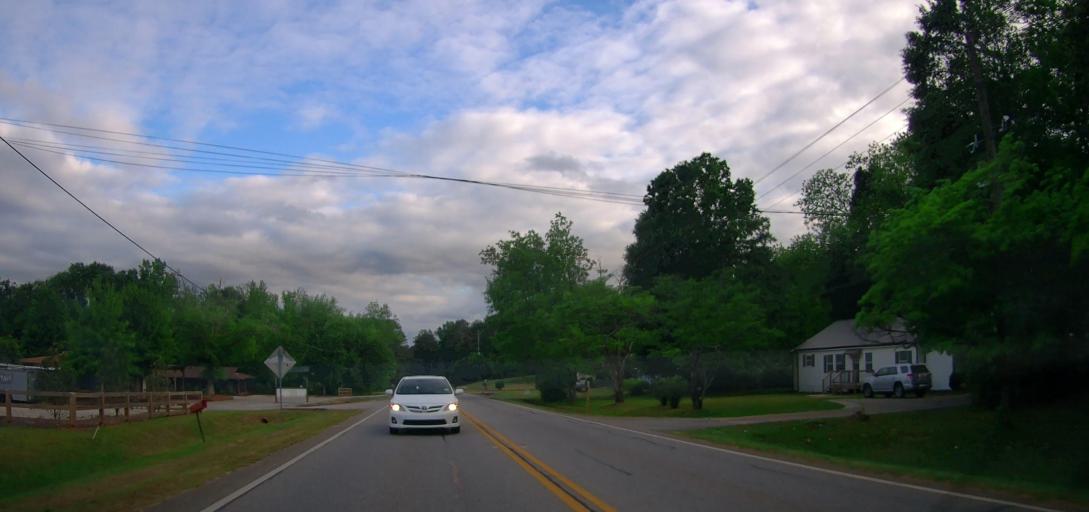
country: US
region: Georgia
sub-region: Oconee County
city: Watkinsville
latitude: 33.8767
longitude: -83.4126
